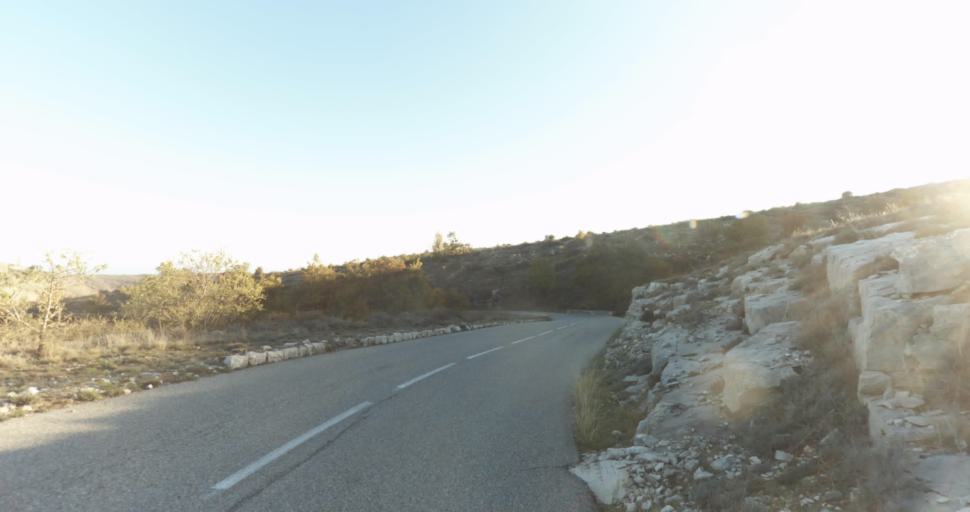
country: FR
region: Provence-Alpes-Cote d'Azur
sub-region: Departement des Alpes-Maritimes
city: Vence
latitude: 43.7554
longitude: 7.0880
